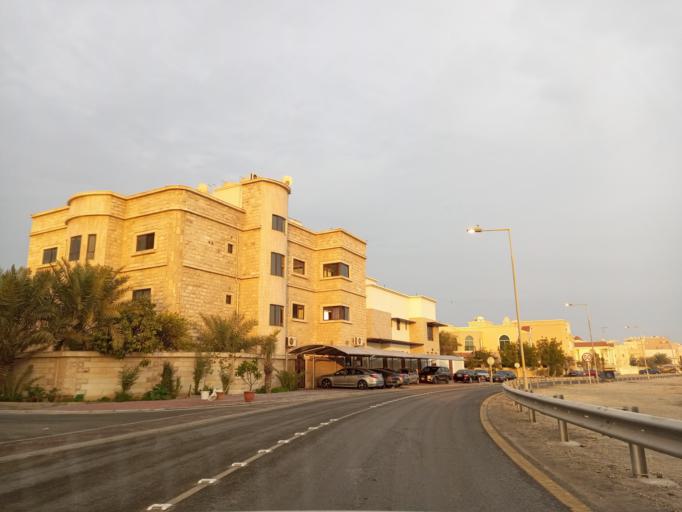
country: BH
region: Muharraq
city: Al Hadd
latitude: 26.2453
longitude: 50.6448
